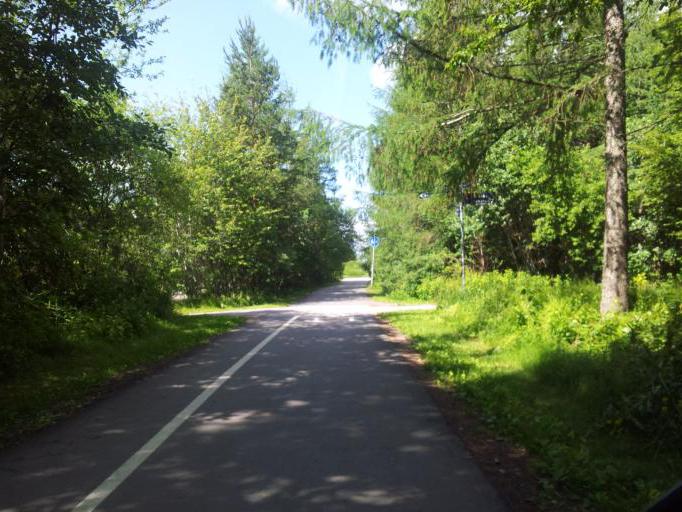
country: SE
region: Uppsala
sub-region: Uppsala Kommun
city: Uppsala
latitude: 59.8785
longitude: 17.6606
